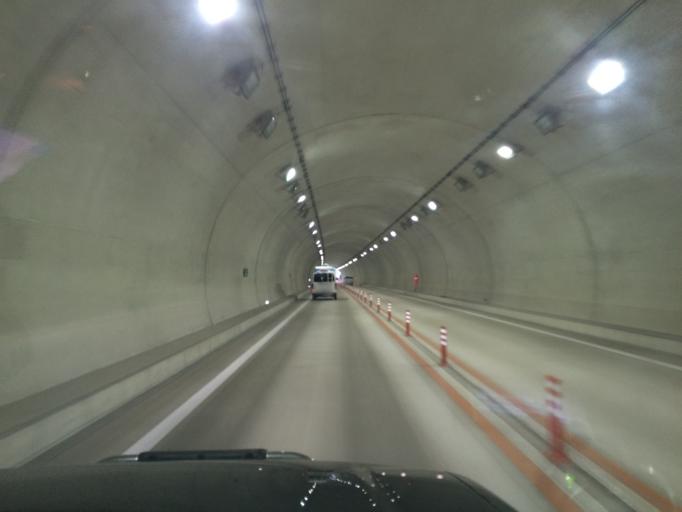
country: JP
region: Tottori
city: Tottori
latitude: 35.4984
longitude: 134.0437
